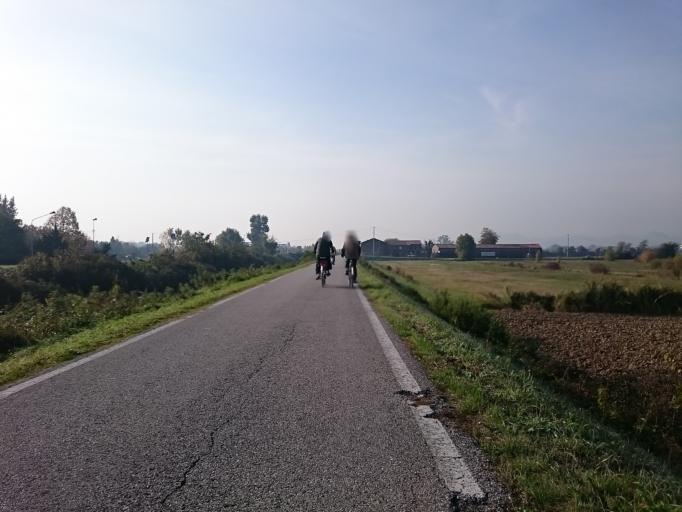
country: IT
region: Veneto
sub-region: Provincia di Padova
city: Mandriola-Sant'Agostino
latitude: 45.3553
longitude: 11.8355
